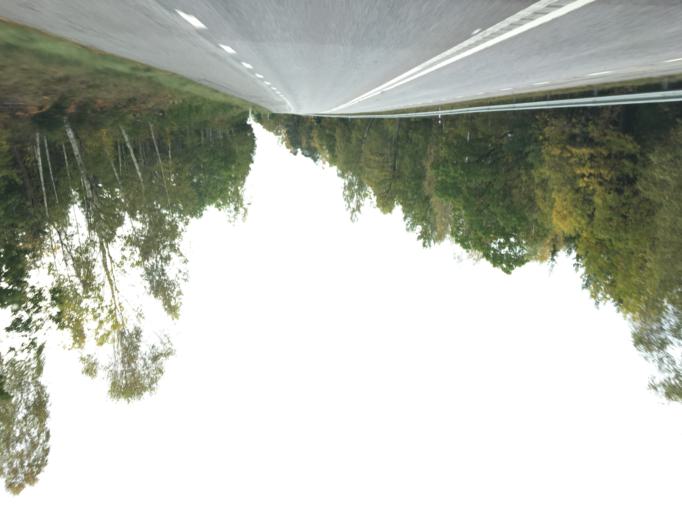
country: SE
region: Soedermanland
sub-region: Nykopings Kommun
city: Stigtomta
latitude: 58.8405
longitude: 16.7408
